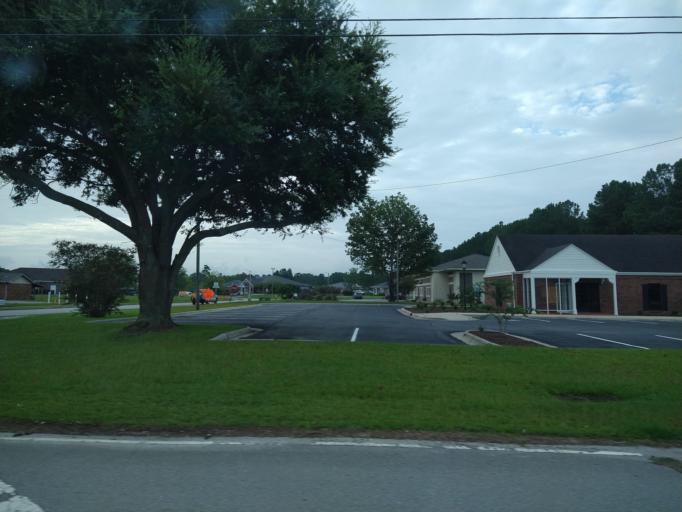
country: US
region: North Carolina
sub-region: Onslow County
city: Pumpkin Center
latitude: 34.7682
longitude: -77.3795
